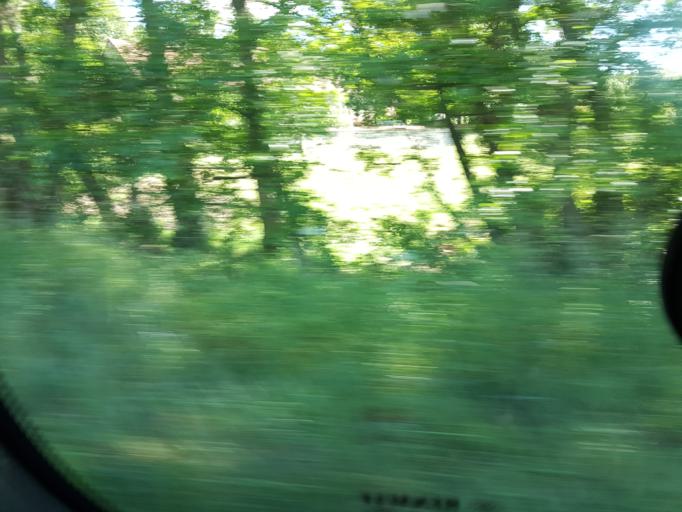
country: FR
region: Bourgogne
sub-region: Departement de Saone-et-Loire
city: Epinac
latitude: 47.0104
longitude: 4.4538
